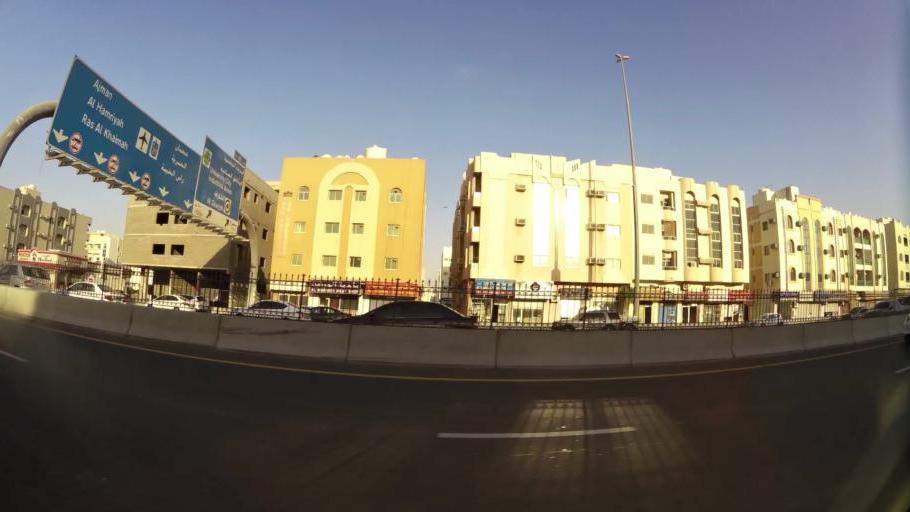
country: AE
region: Ash Shariqah
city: Sharjah
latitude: 25.3019
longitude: 55.4410
